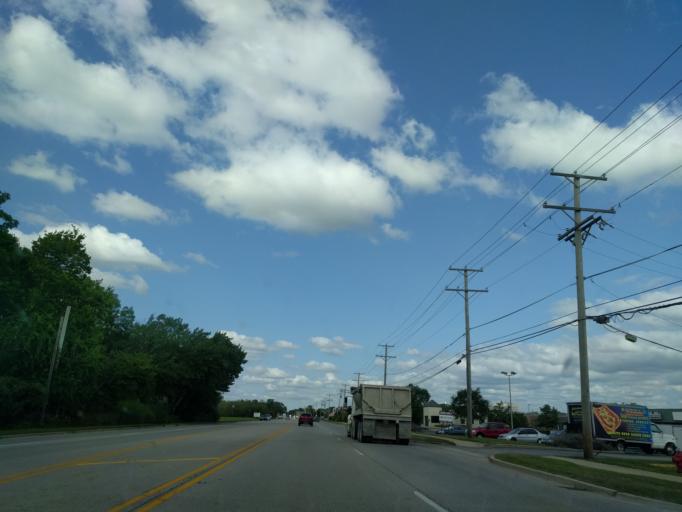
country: US
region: Illinois
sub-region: Cook County
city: Elk Grove Village
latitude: 42.0265
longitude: -87.9715
